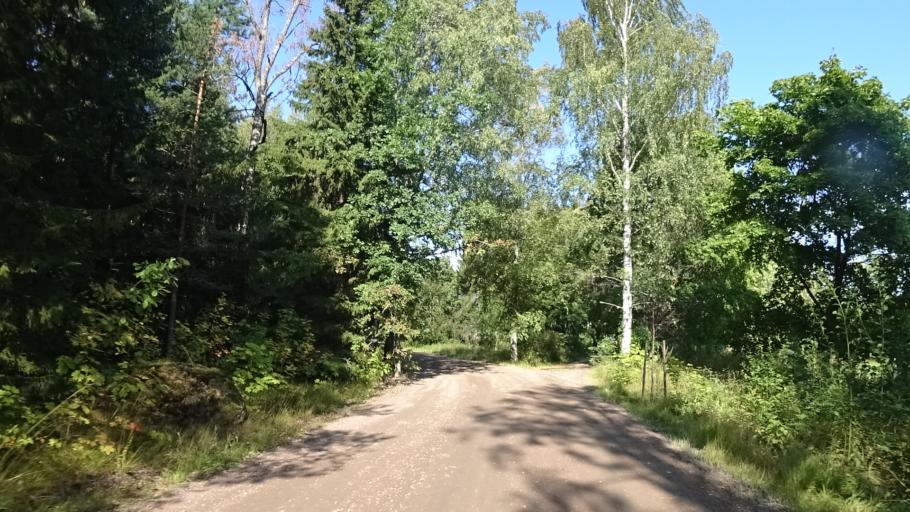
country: FI
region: Kymenlaakso
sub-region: Kotka-Hamina
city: Hamina
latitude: 60.5397
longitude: 27.2213
